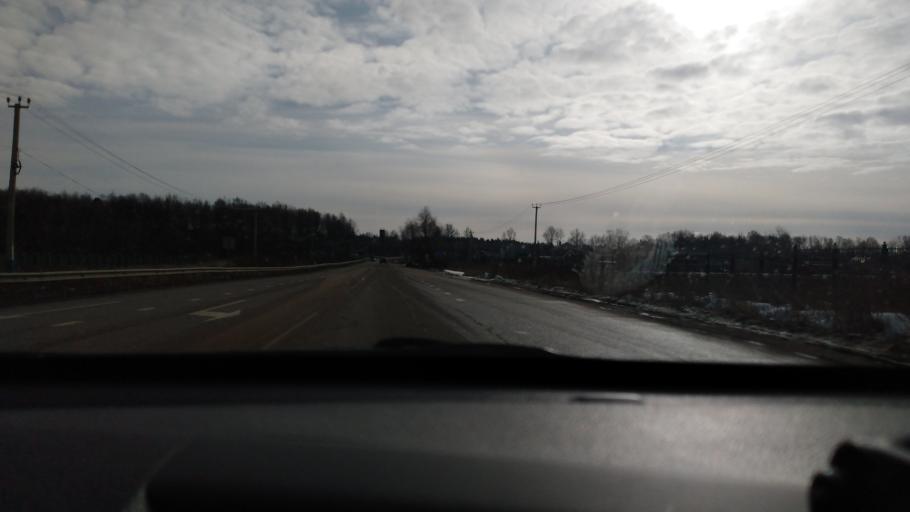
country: RU
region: Moskovskaya
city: Nakhabino
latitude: 55.8891
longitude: 37.1847
